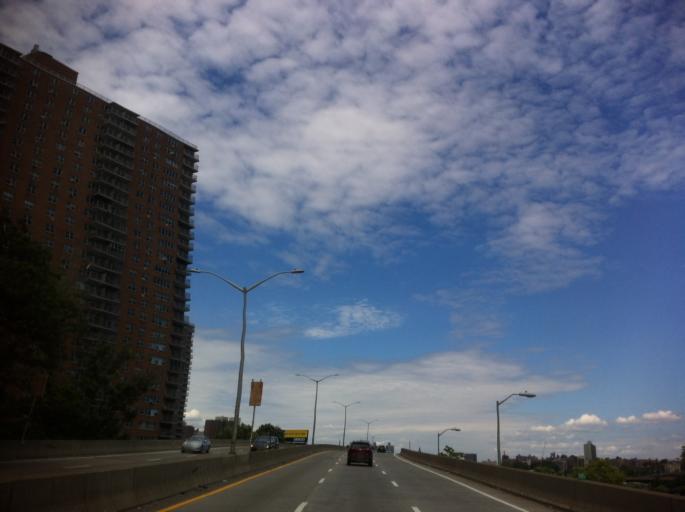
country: US
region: New Jersey
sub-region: Bergen County
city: Edgewater
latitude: 40.8202
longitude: -73.9345
